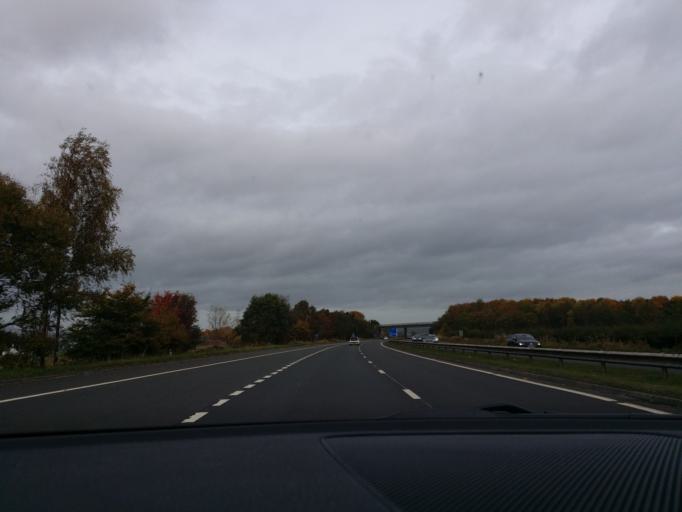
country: GB
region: Scotland
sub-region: Falkirk
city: Airth
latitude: 56.0483
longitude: -3.7769
